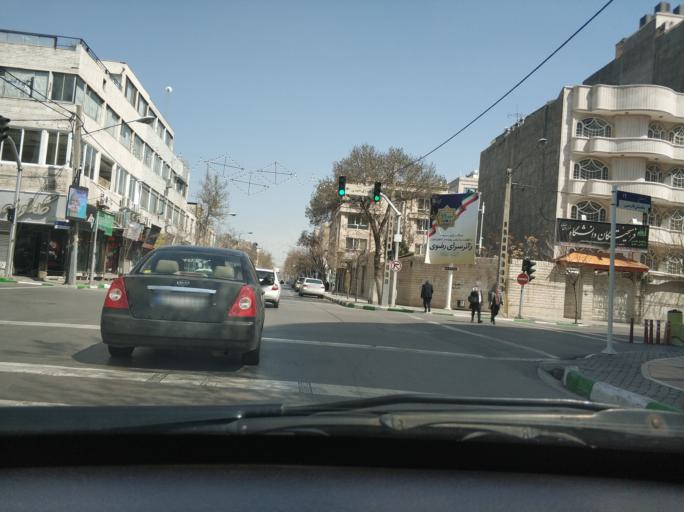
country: IR
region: Razavi Khorasan
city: Mashhad
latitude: 36.3040
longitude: 59.5715
